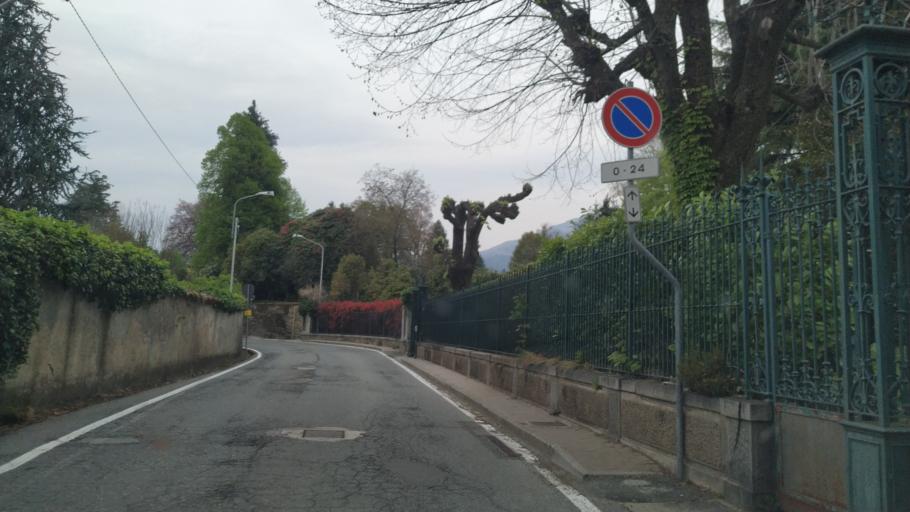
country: IT
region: Piedmont
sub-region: Provincia di Biella
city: Pollone
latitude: 45.5812
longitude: 8.0063
